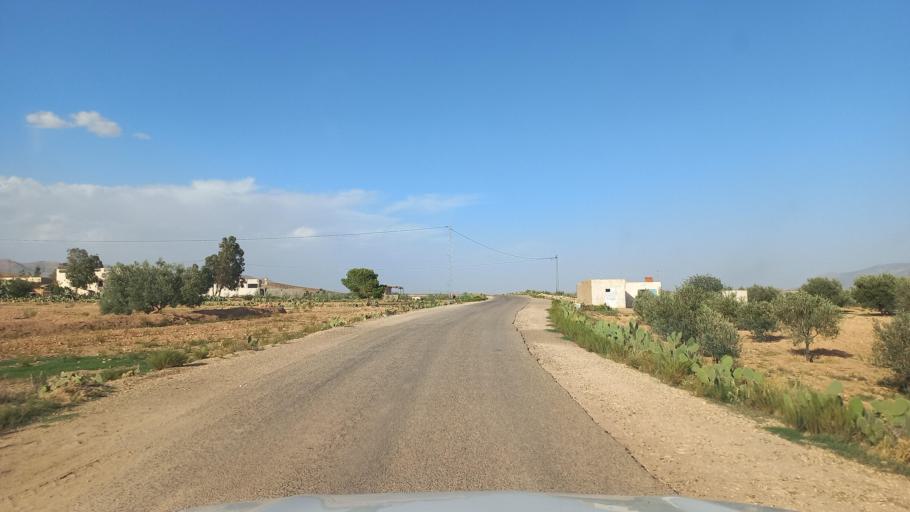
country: TN
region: Al Qasrayn
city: Sbiba
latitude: 35.3736
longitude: 9.0140
